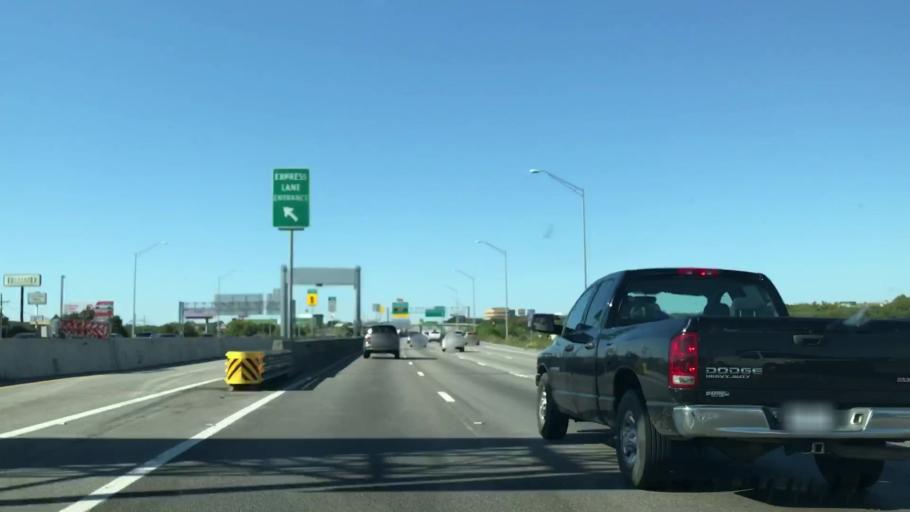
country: US
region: Texas
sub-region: Denton County
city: Lewisville
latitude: 33.0119
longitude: -96.9784
